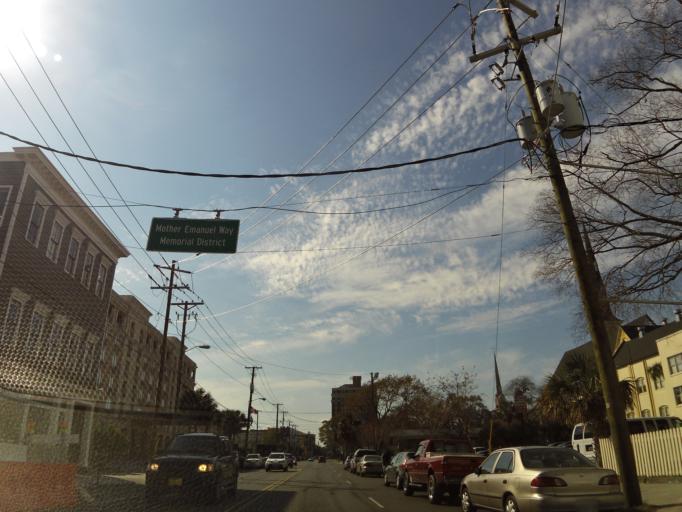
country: US
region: South Carolina
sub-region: Charleston County
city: Charleston
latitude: 32.7872
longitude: -79.9331
